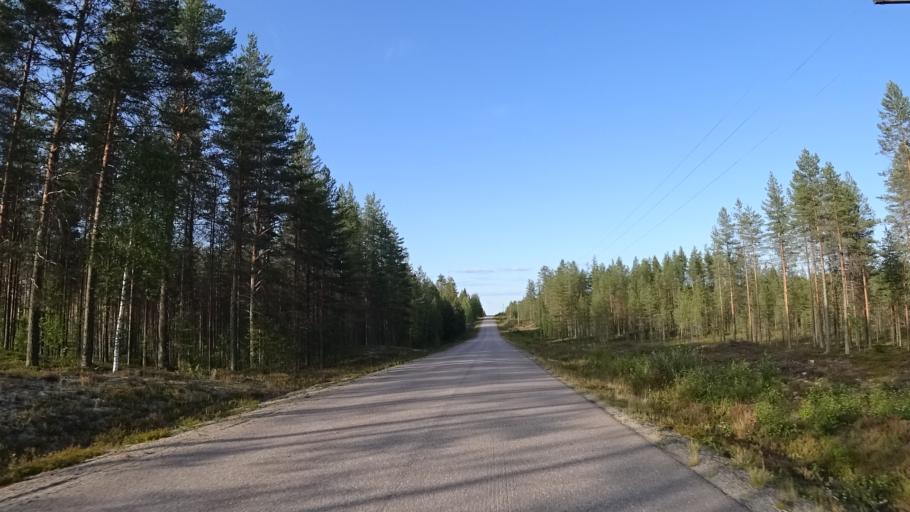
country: FI
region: North Karelia
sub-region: Joensuu
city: Eno
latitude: 63.0675
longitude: 30.5622
